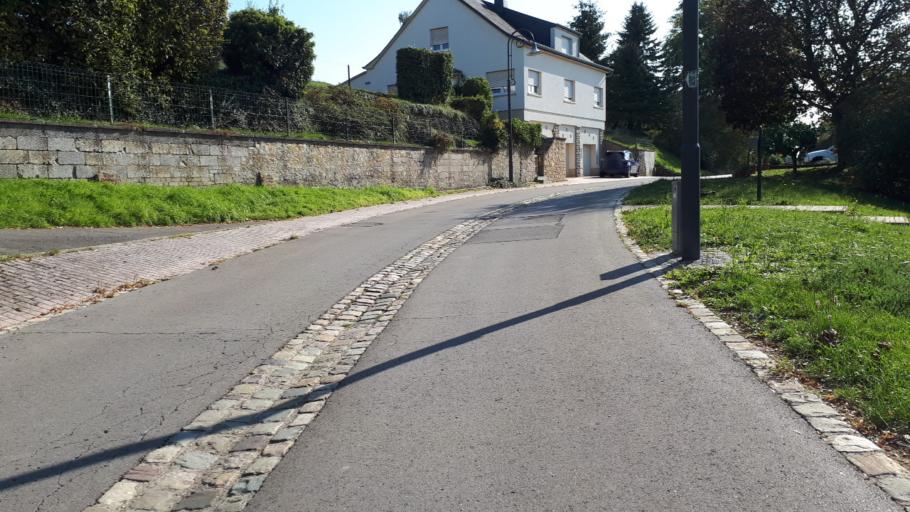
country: LU
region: Luxembourg
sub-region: Canton de Capellen
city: Kehlen
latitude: 49.6647
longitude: 6.0339
